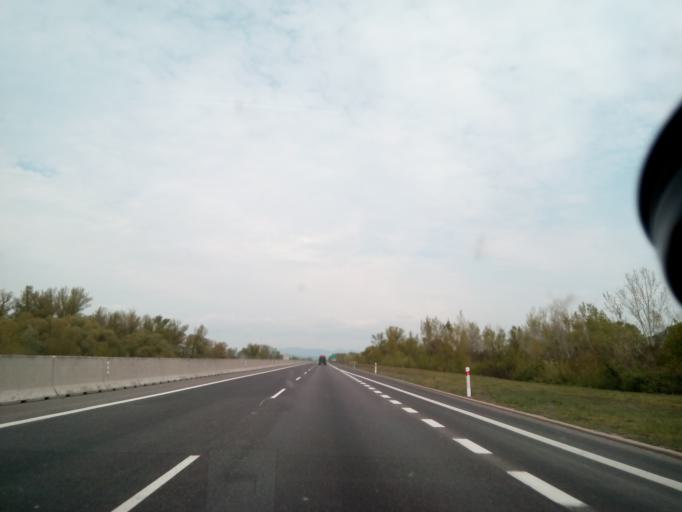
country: SK
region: Trenciansky
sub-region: Okres Nove Mesto nad Vahom
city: Nove Mesto nad Vahom
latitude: 48.6788
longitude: 17.8729
